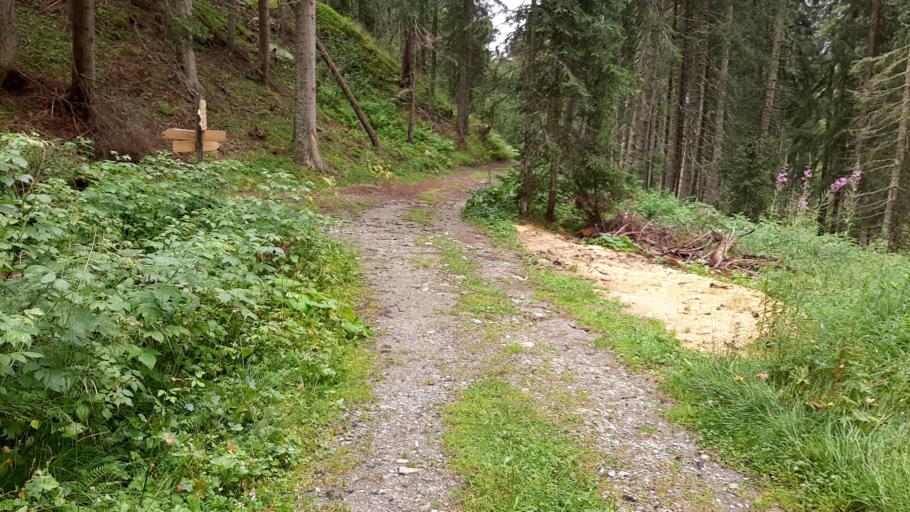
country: IT
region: Trentino-Alto Adige
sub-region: Bolzano
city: Sesto
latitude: 46.6983
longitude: 12.3796
